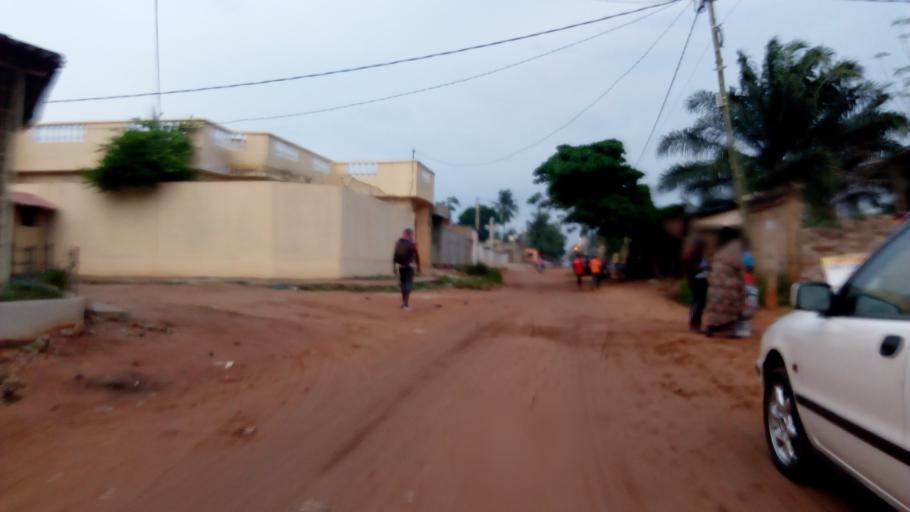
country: TG
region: Maritime
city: Lome
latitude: 6.2152
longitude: 1.2061
